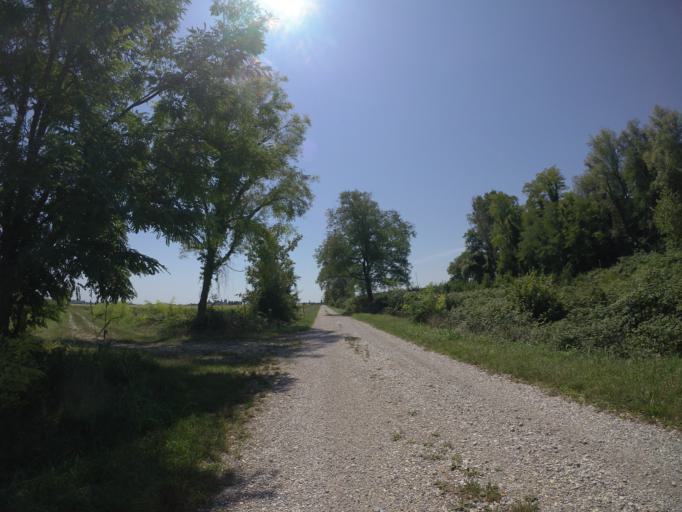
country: IT
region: Friuli Venezia Giulia
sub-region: Provincia di Udine
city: Varmo
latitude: 45.9190
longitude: 13.0027
